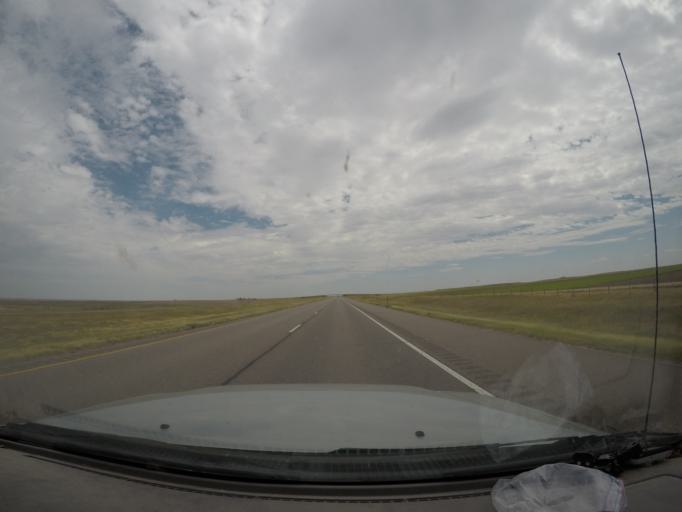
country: US
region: Nebraska
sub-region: Kimball County
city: Kimball
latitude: 41.1918
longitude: -103.8134
